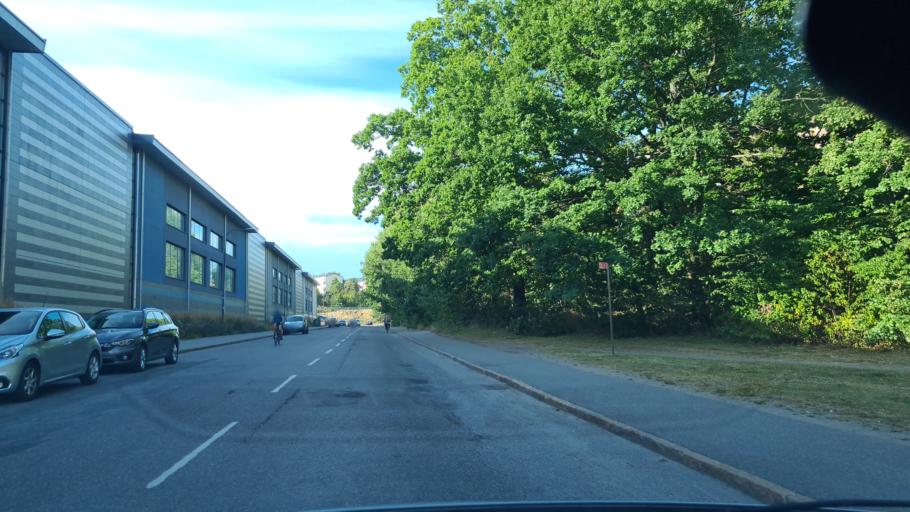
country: SE
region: Stockholm
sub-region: Stockholms Kommun
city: Arsta
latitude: 59.2917
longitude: 18.0956
